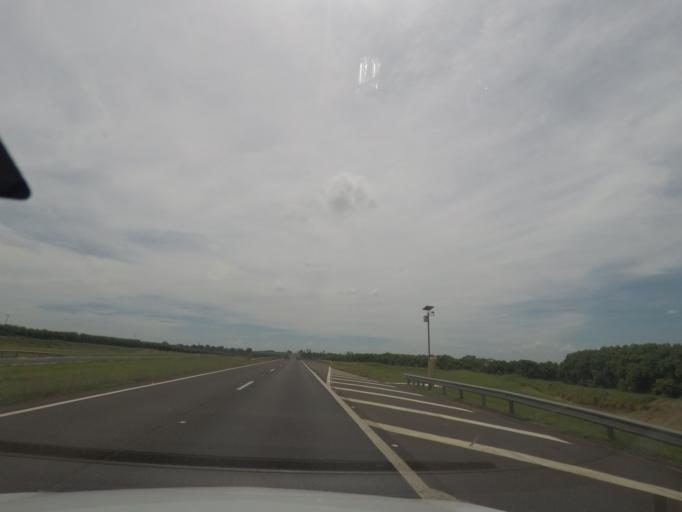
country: BR
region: Sao Paulo
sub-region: Bebedouro
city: Bebedouro
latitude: -21.0096
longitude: -48.4275
